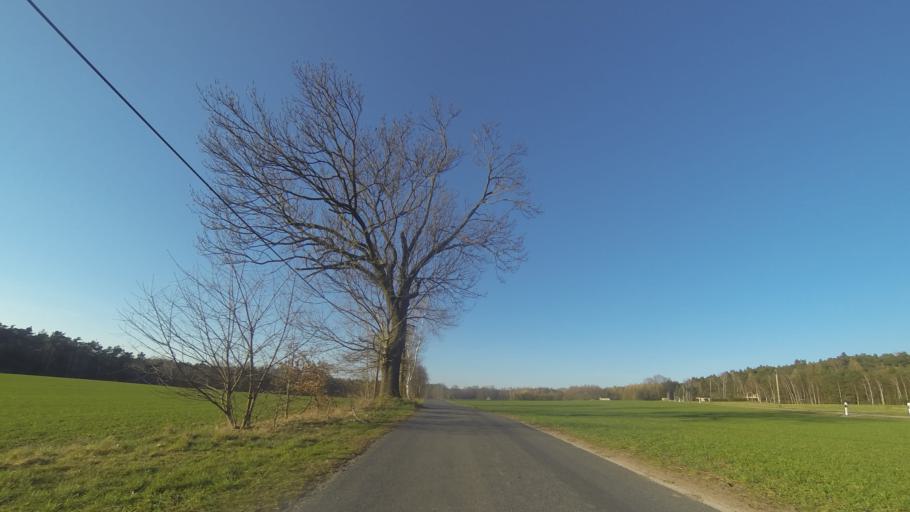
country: DE
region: Saxony
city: Ottendorf-Okrilla
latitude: 51.1902
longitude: 13.7947
